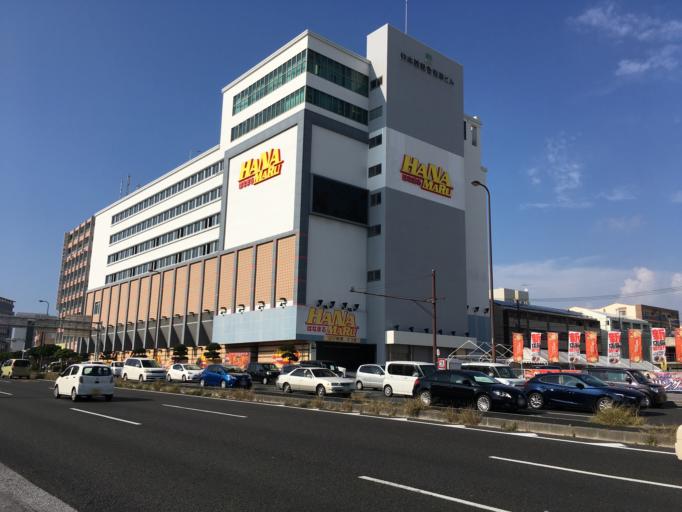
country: JP
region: Okinawa
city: Naha-shi
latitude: 26.2307
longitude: 127.6859
